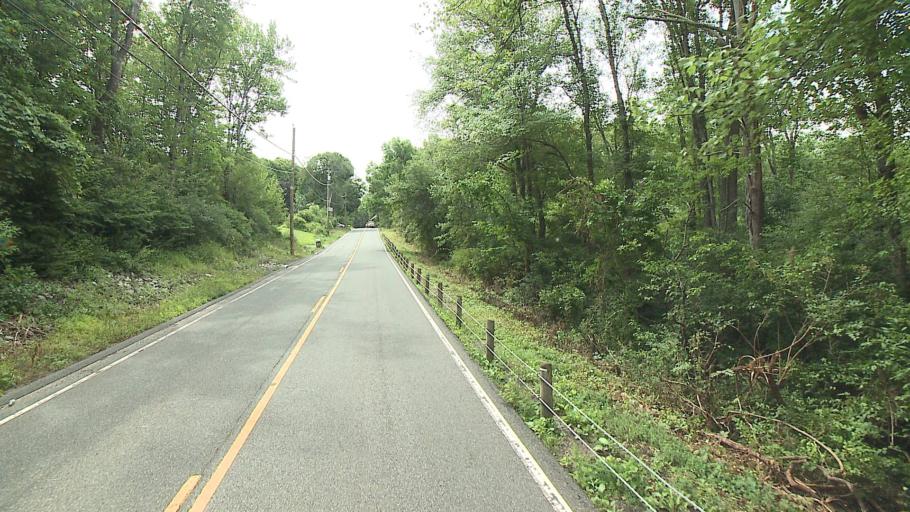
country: US
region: Connecticut
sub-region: Litchfield County
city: Bethlehem Village
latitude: 41.6083
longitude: -73.2872
